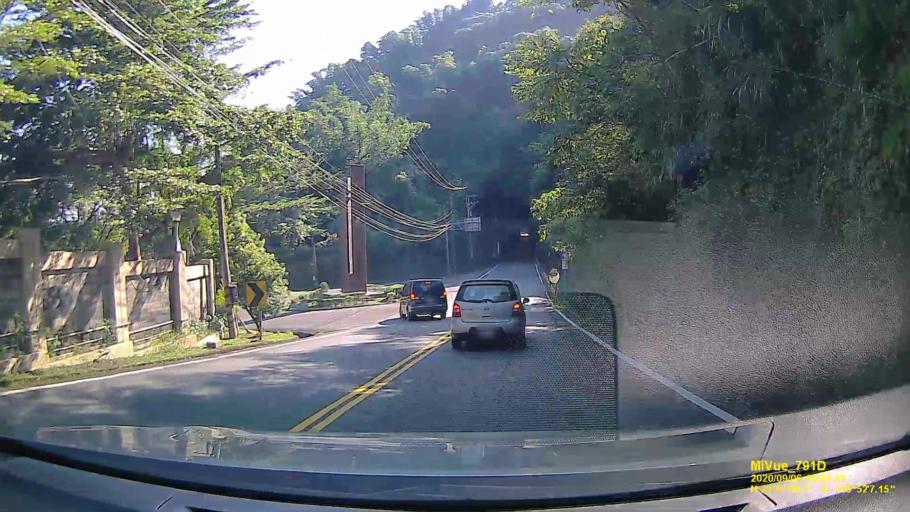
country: TW
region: Taiwan
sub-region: Nantou
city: Puli
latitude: 23.8546
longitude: 120.8686
